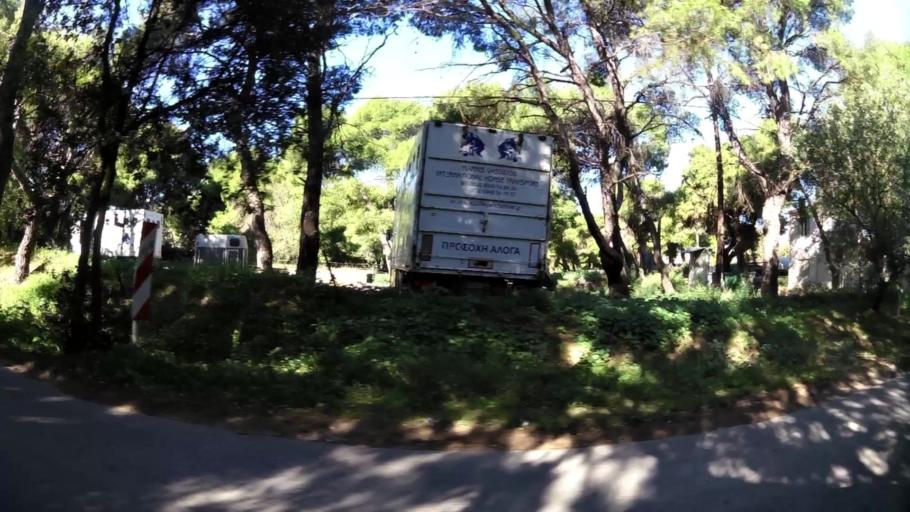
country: GR
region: Attica
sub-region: Nomarchia Anatolikis Attikis
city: Varybobi
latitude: 38.1255
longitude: 23.7938
